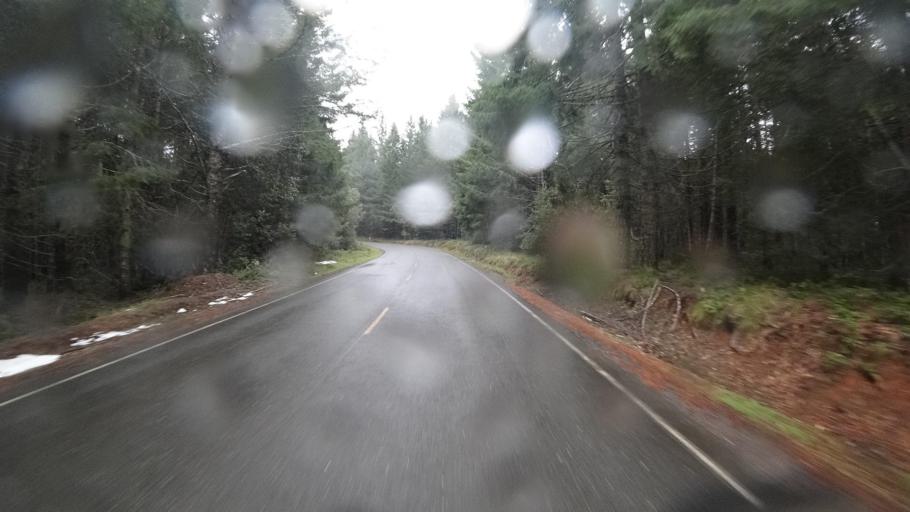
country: US
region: California
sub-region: Humboldt County
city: Willow Creek
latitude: 41.1775
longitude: -123.8161
